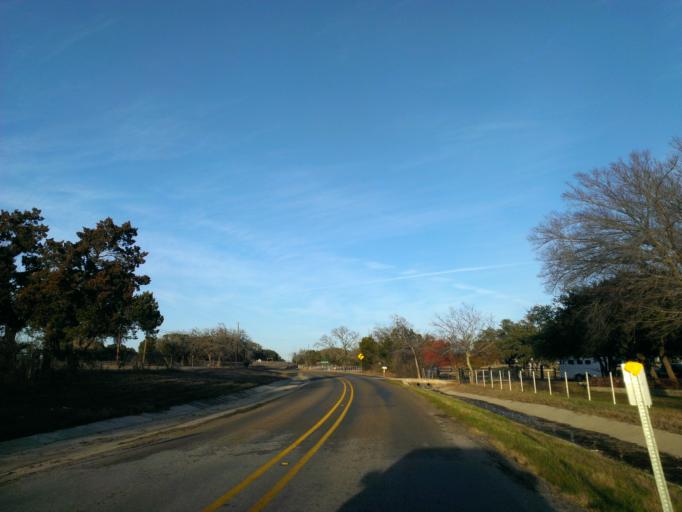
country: US
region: Texas
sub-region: Burnet County
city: Bertram
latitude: 30.7283
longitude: -98.0844
